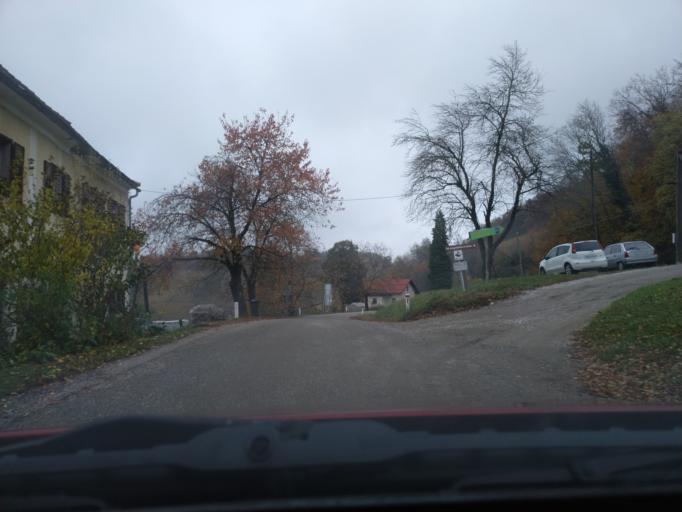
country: SI
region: Sentilj
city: Sentilj v Slov. Goricah
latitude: 46.6798
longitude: 15.6143
